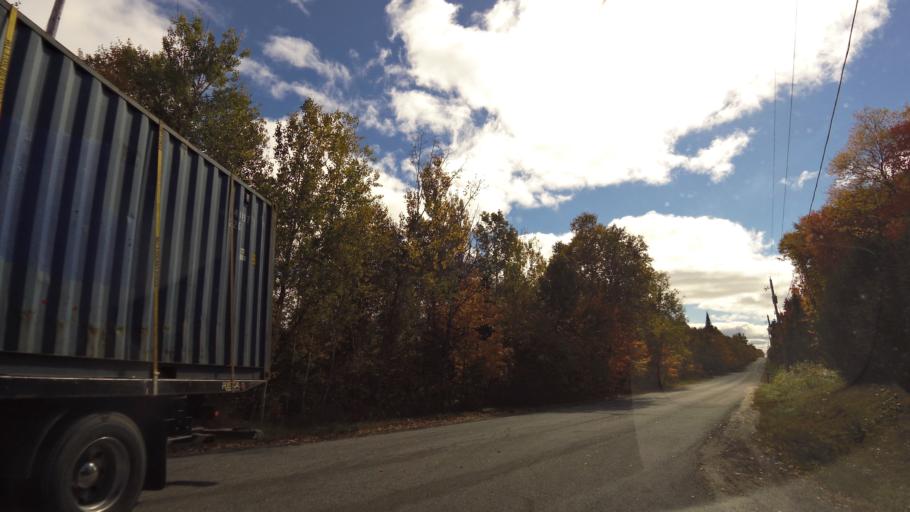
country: CA
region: Ontario
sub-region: Nipissing District
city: North Bay
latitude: 46.3760
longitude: -79.4871
